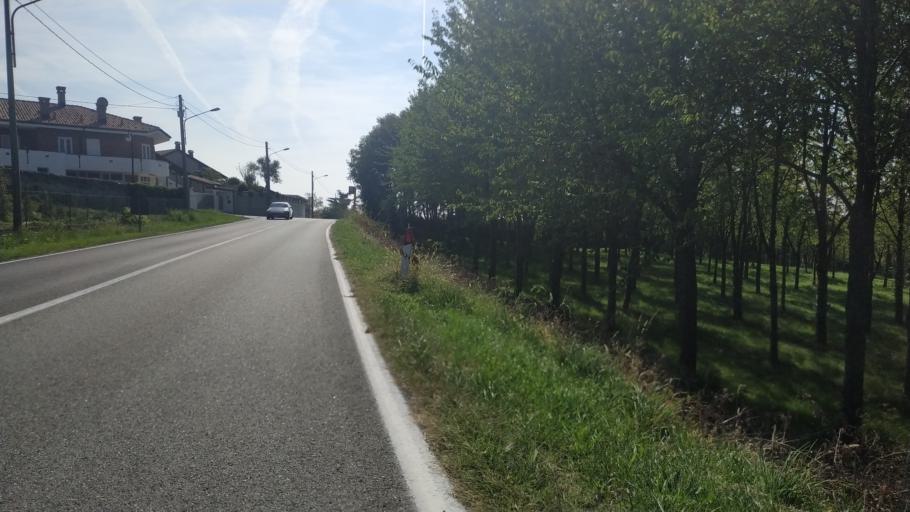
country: IT
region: Piedmont
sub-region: Provincia di Torino
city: Orio Canavese
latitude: 45.3312
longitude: 7.8555
